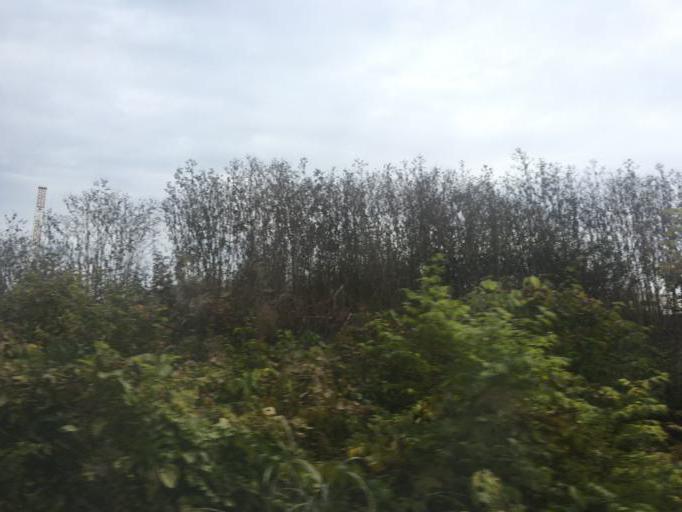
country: JP
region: Tokyo
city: Fussa
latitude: 35.7842
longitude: 139.3420
